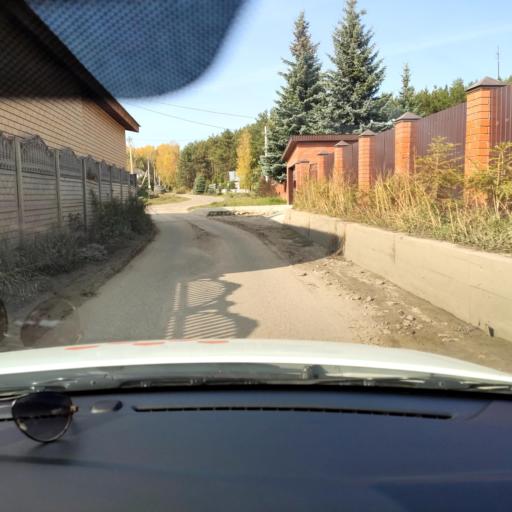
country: RU
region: Tatarstan
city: Stolbishchi
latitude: 55.6791
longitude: 49.1165
